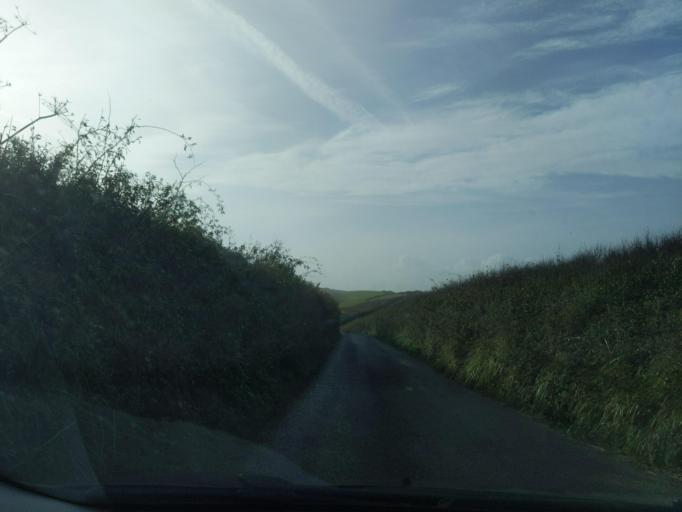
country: GB
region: England
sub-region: Cornwall
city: Pillaton
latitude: 50.3640
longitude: -4.3205
